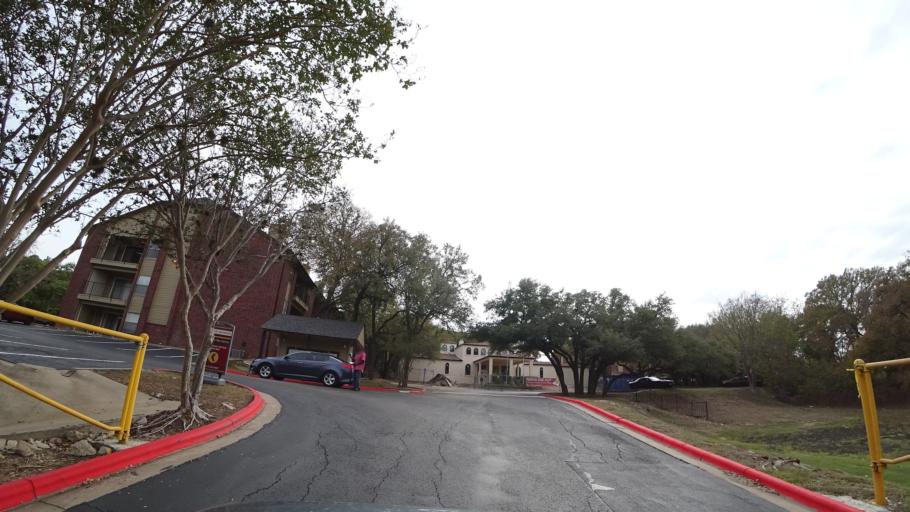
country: US
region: Texas
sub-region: Williamson County
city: Round Rock
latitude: 30.5163
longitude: -97.6626
